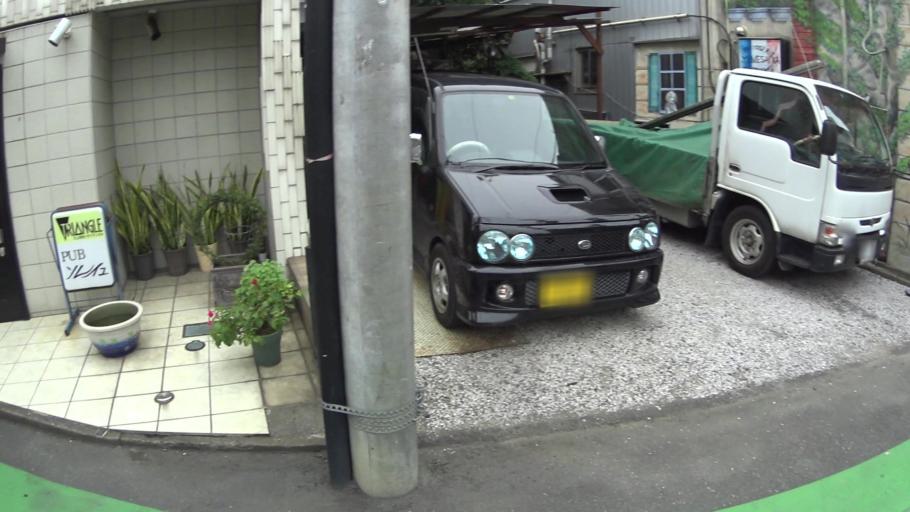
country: JP
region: Saitama
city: Hanno
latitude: 35.8538
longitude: 139.3174
